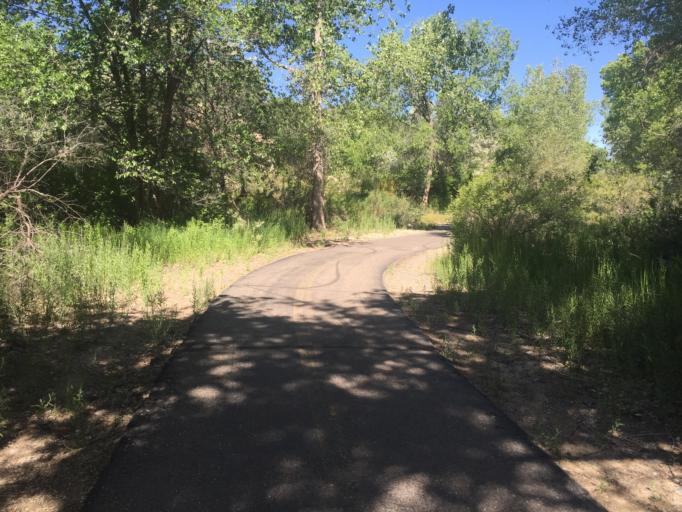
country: US
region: Colorado
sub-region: Mesa County
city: Redlands
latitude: 39.0737
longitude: -108.6043
